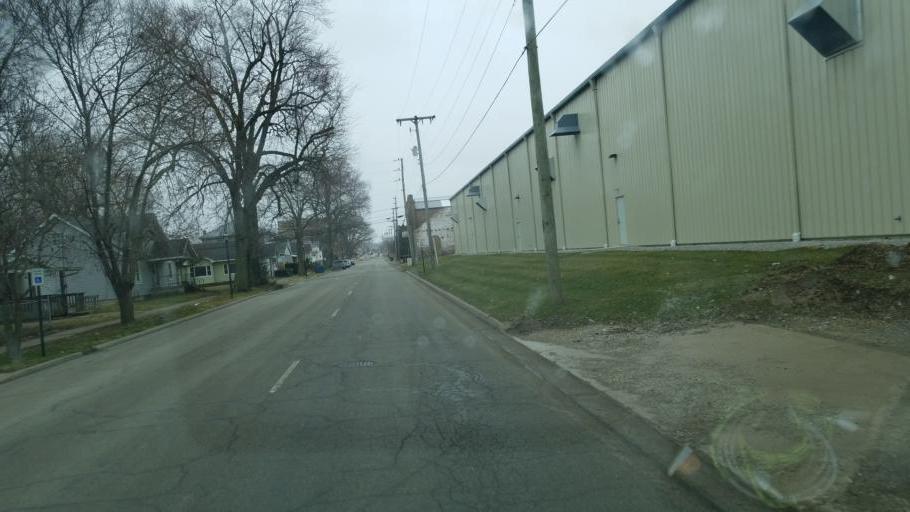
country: US
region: Indiana
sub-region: Wabash County
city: Wabash
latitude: 40.7952
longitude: -85.8299
